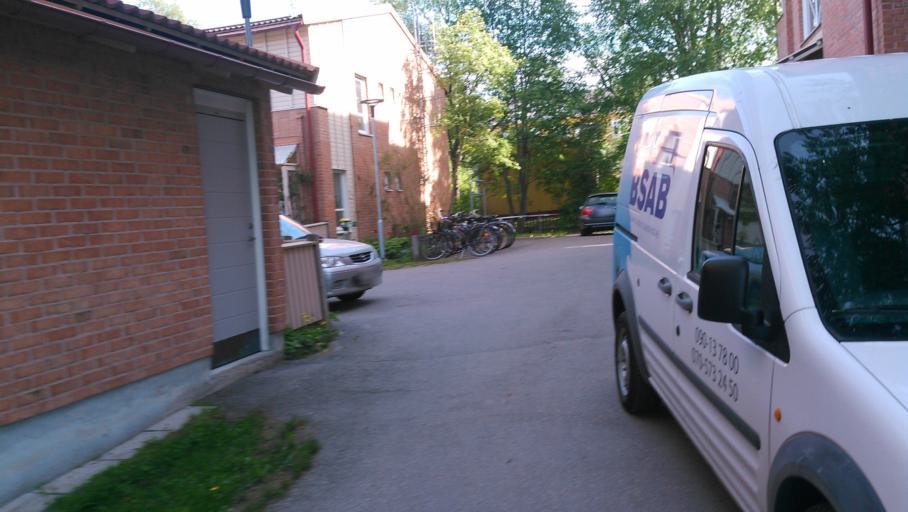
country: SE
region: Vaesterbotten
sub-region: Umea Kommun
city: Umea
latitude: 63.8189
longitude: 20.2832
